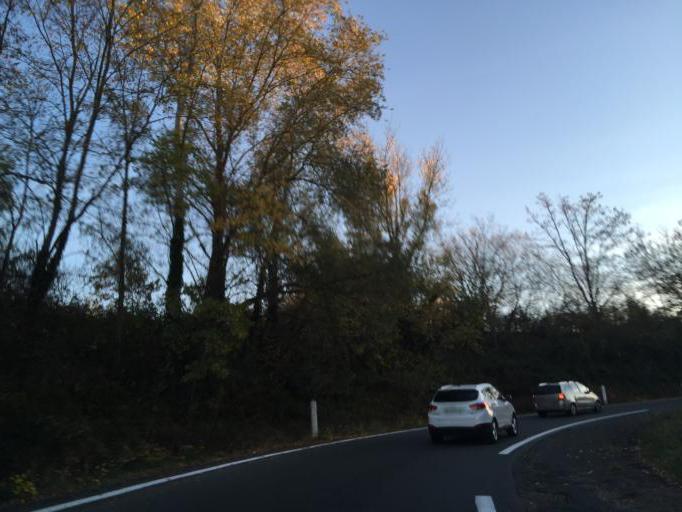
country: FR
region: Rhone-Alpes
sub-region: Departement de la Loire
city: Le Coteau
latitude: 46.0184
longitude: 4.1028
